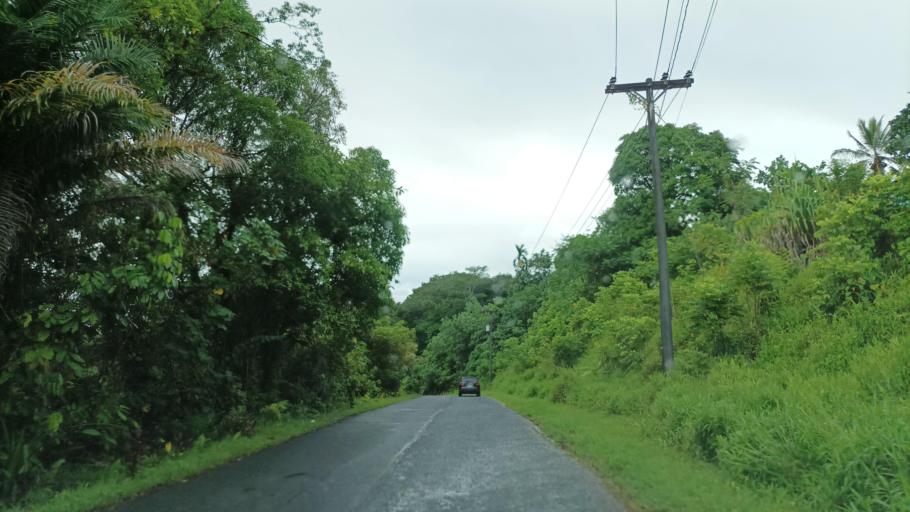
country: FM
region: Pohnpei
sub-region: Sokehs Municipality
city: Palikir - National Government Center
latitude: 6.8807
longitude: 158.1603
